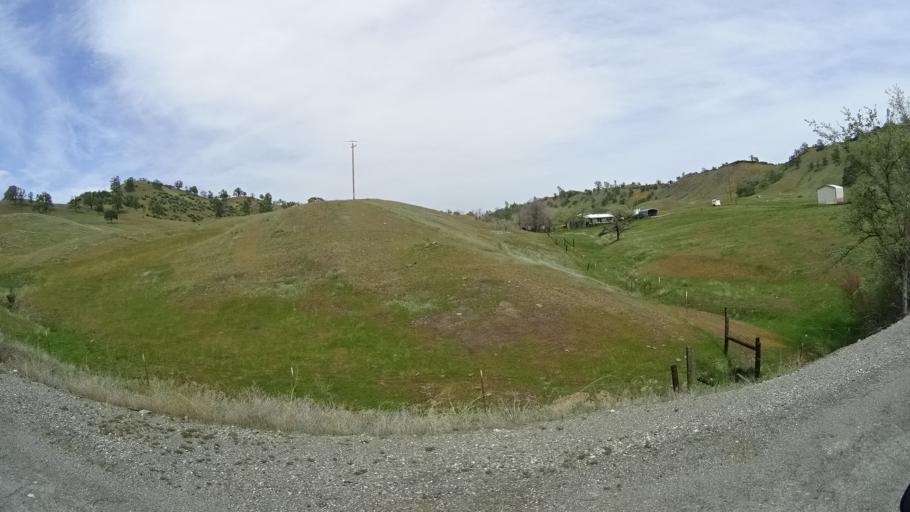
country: US
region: California
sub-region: Glenn County
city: Willows
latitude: 39.6158
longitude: -122.5881
